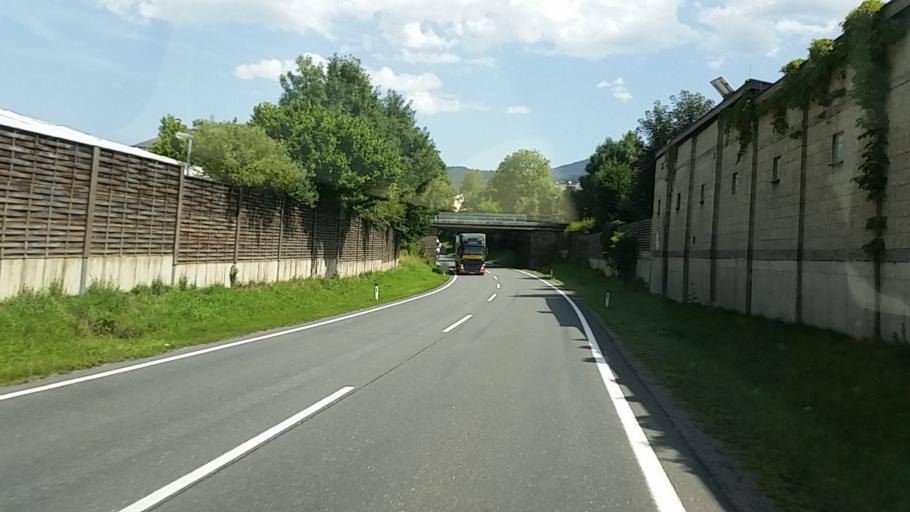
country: AT
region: Salzburg
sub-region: Politischer Bezirk Sankt Johann im Pongau
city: Radstadt
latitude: 47.3861
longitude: 13.4593
